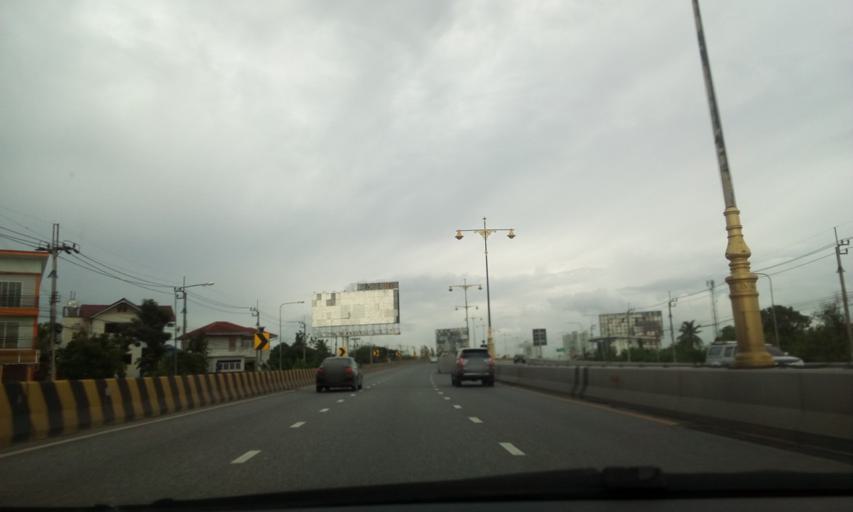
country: TH
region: Nonthaburi
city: Pak Kret
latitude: 13.9202
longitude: 100.4890
